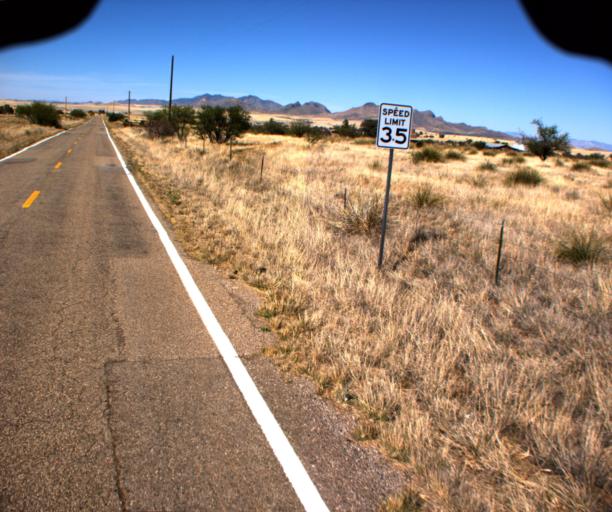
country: US
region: Arizona
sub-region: Cochise County
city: Huachuca City
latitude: 31.5924
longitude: -110.5600
